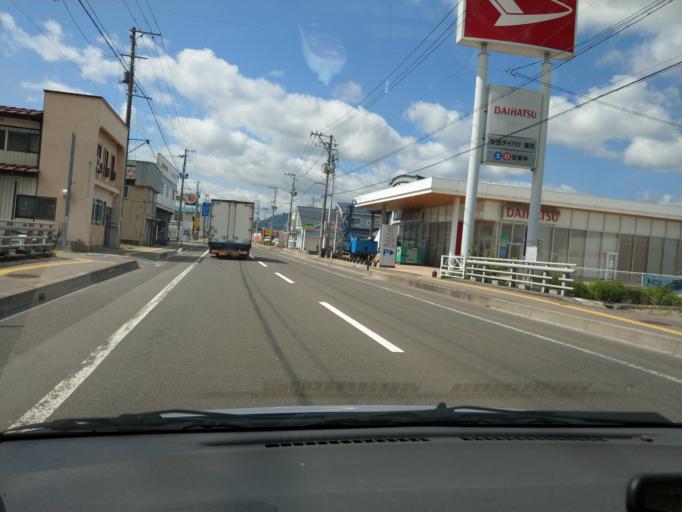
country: JP
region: Akita
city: Yuzawa
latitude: 39.1714
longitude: 140.4910
